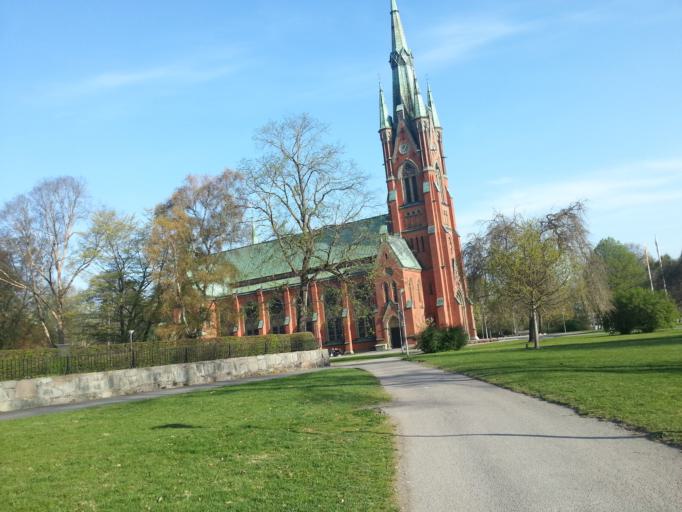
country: SE
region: OEstergoetland
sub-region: Norrkopings Kommun
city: Norrkoping
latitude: 58.5923
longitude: 16.1727
